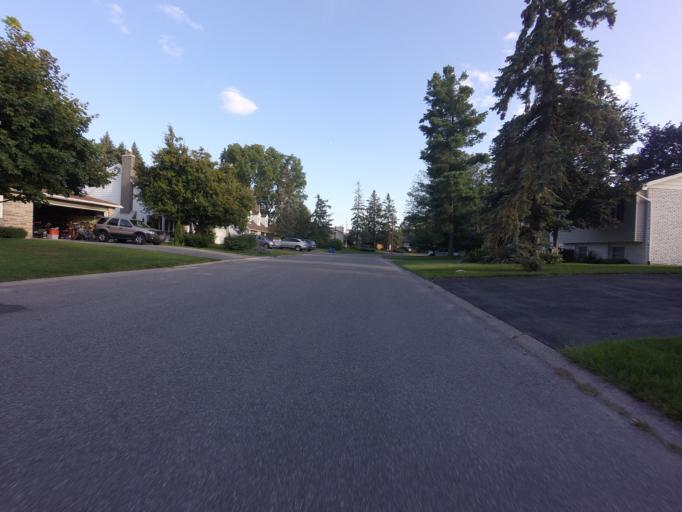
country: CA
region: Ontario
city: Bells Corners
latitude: 45.3377
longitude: -75.7742
